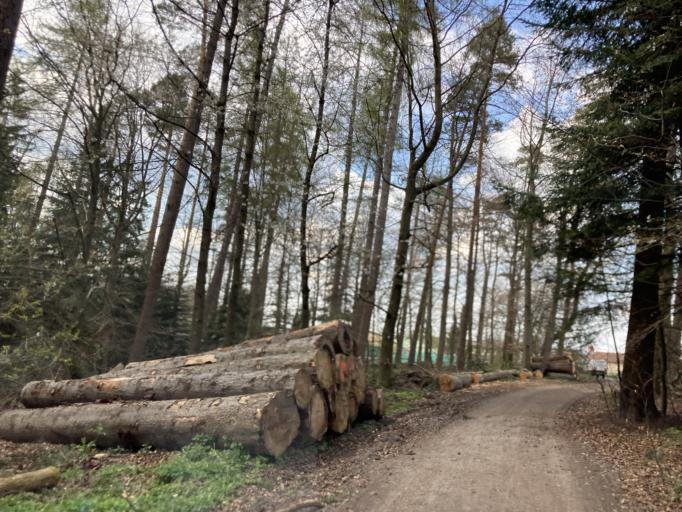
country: DE
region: Baden-Wuerttemberg
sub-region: Karlsruhe Region
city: Dobel
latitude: 48.8393
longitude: 8.5183
